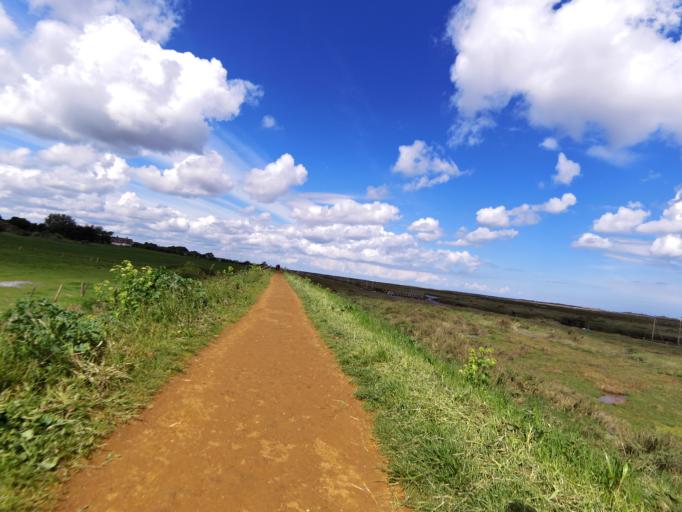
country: GB
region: England
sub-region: Norfolk
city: Briston
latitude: 52.9569
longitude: 0.9928
